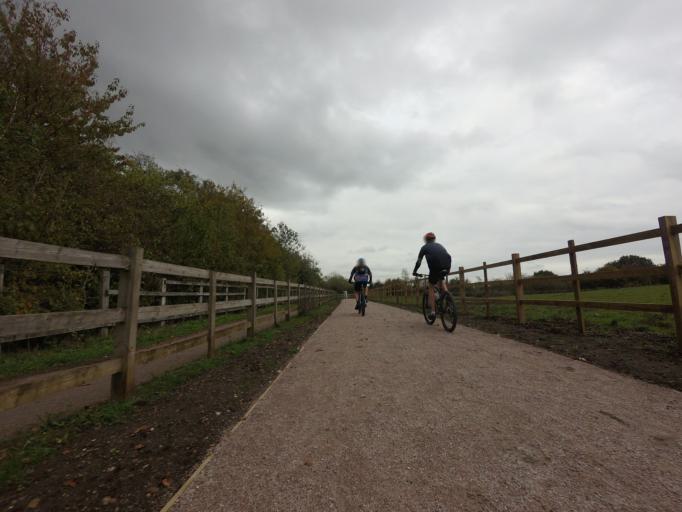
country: GB
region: England
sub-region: Kent
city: Swanley
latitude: 51.3900
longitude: 0.1669
